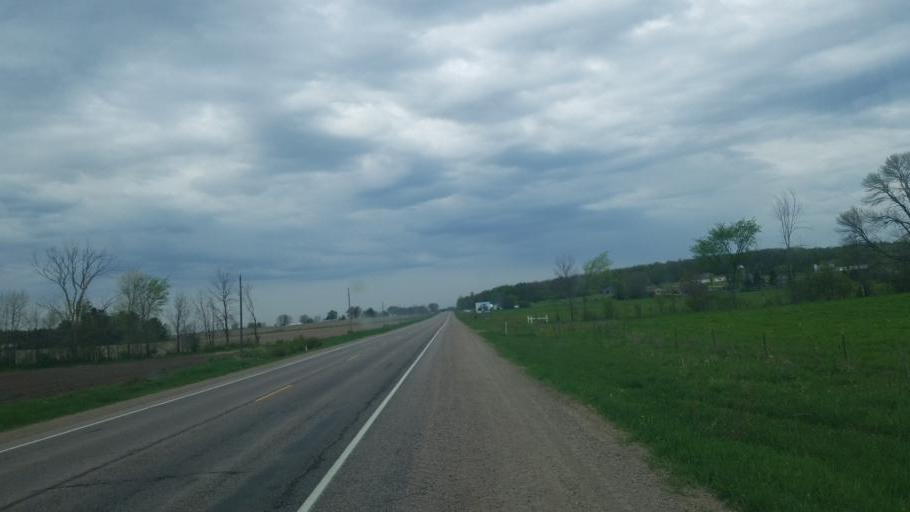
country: US
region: Wisconsin
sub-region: Marathon County
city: Spencer
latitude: 44.5988
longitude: -90.3298
